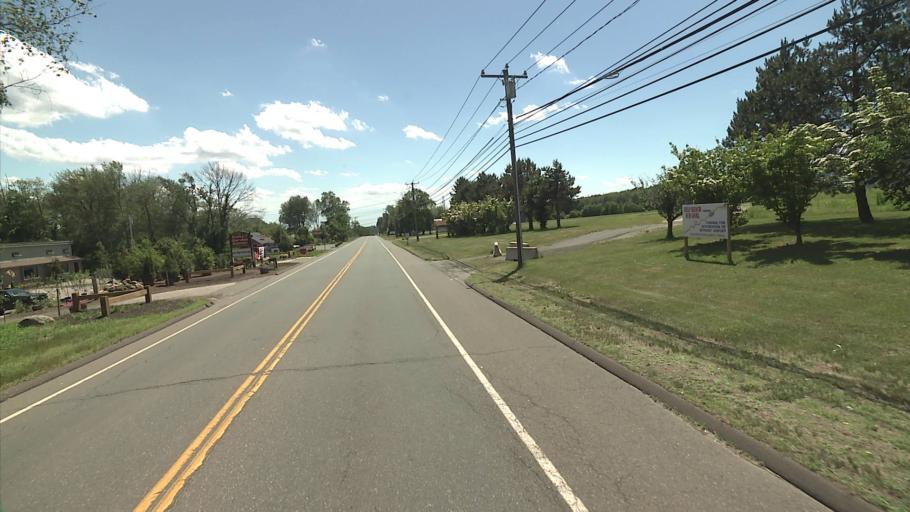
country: US
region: Connecticut
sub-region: New Haven County
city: Prospect
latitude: 41.4395
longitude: -72.9912
